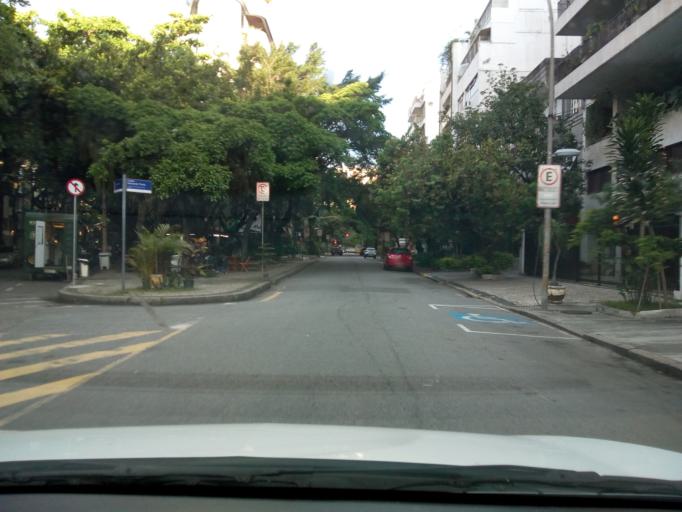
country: BR
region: Rio de Janeiro
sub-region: Rio De Janeiro
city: Rio de Janeiro
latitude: -22.9811
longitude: -43.2047
